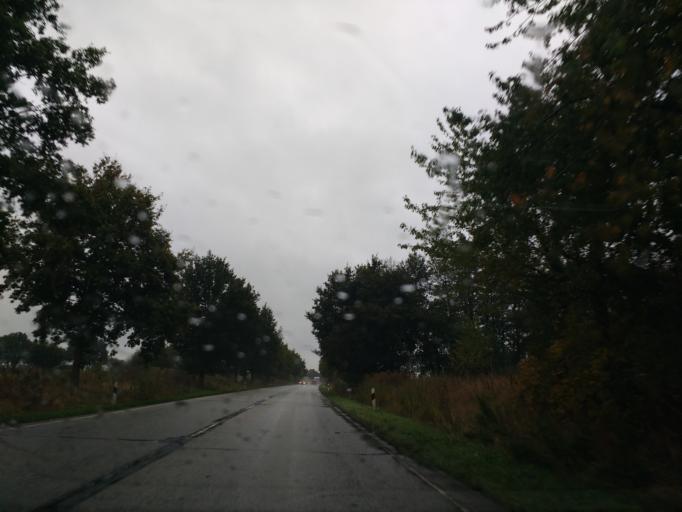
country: DE
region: Schleswig-Holstein
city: Susel
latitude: 54.0698
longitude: 10.7111
